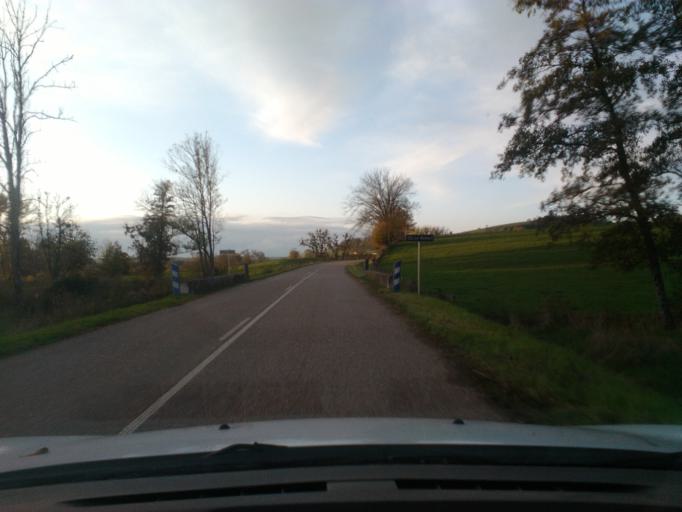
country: FR
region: Lorraine
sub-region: Departement des Vosges
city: Mirecourt
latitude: 48.2523
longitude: 6.1989
